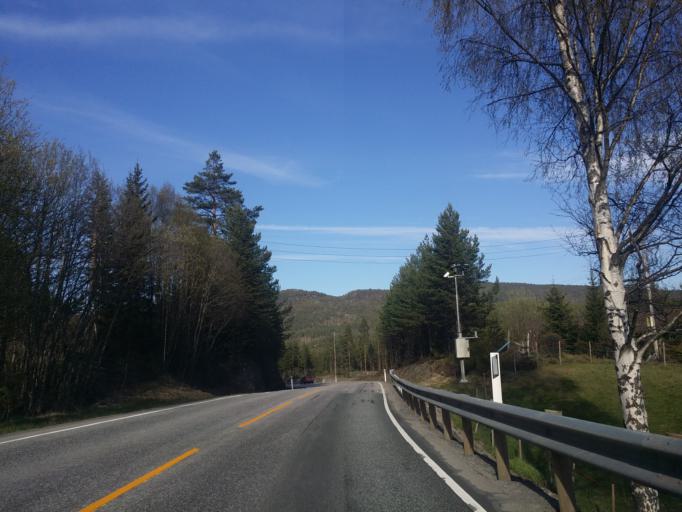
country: NO
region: Telemark
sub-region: Notodden
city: Notodden
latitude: 59.6112
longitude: 9.4541
